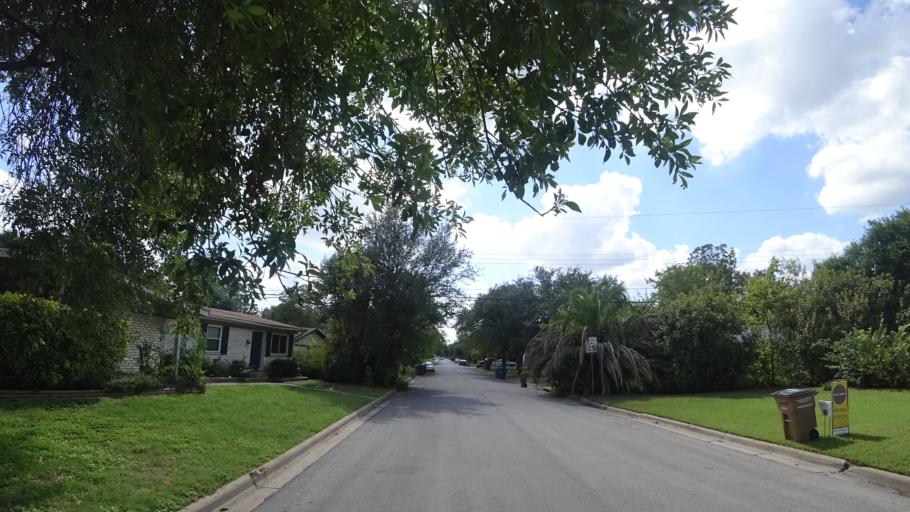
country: US
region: Texas
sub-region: Williamson County
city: Jollyville
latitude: 30.3615
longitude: -97.7279
